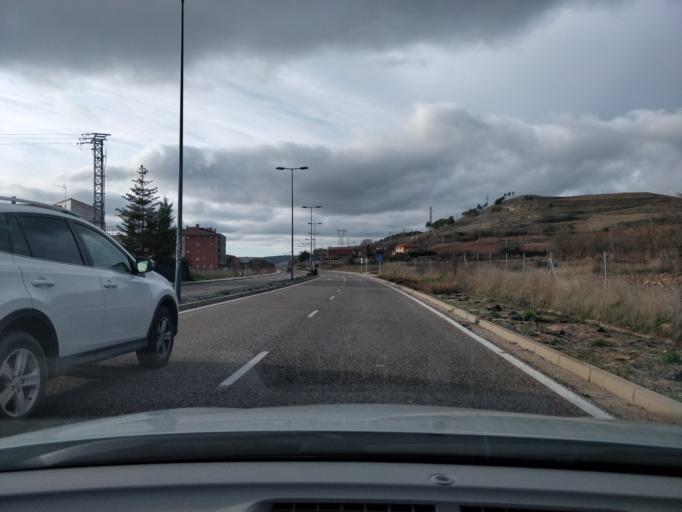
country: ES
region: Castille and Leon
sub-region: Provincia de Burgos
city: Villagonzalo-Pedernales
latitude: 42.3496
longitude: -3.7299
